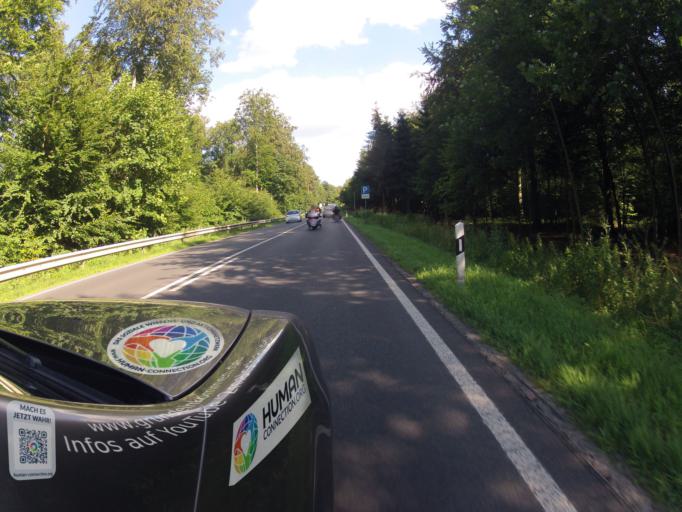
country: DE
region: Mecklenburg-Vorpommern
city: Seebad Bansin
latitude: 53.9740
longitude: 14.1132
